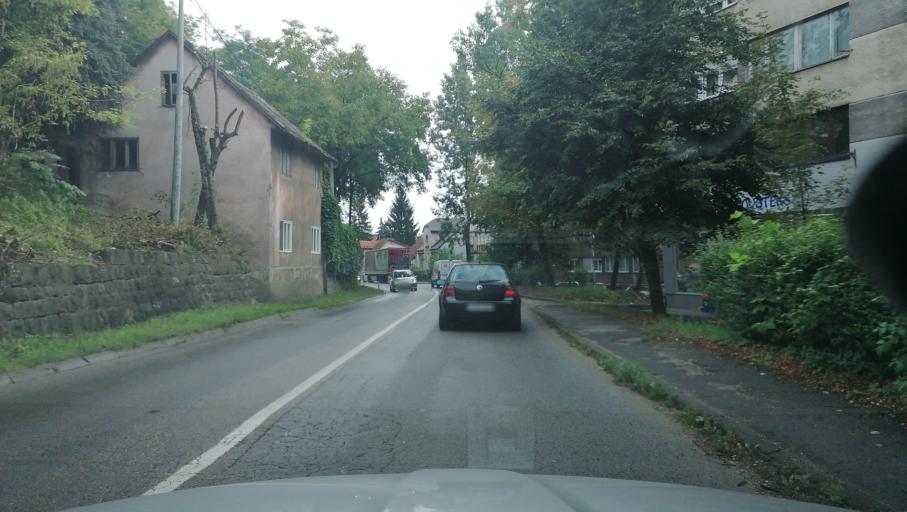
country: BA
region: Republika Srpska
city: Hiseti
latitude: 44.7669
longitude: 17.1793
